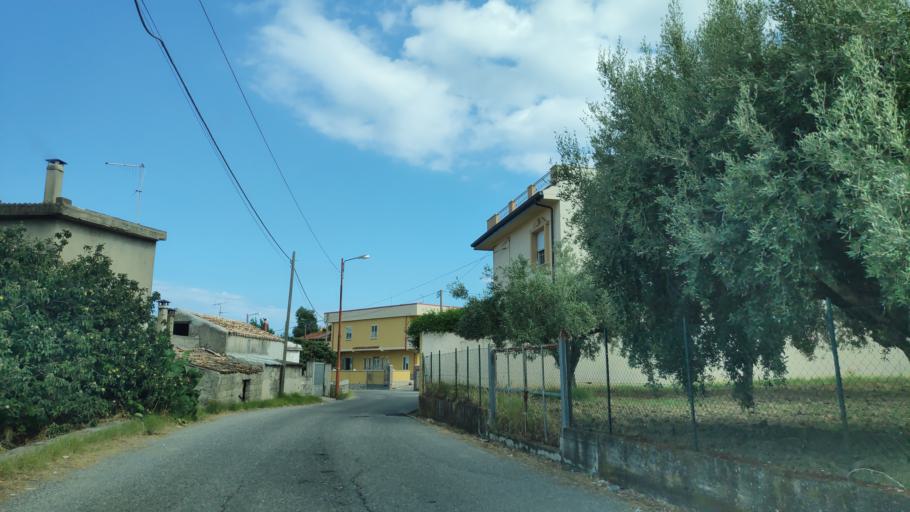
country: IT
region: Calabria
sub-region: Provincia di Catanzaro
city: Guardavalle Marina
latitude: 38.4628
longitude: 16.5763
